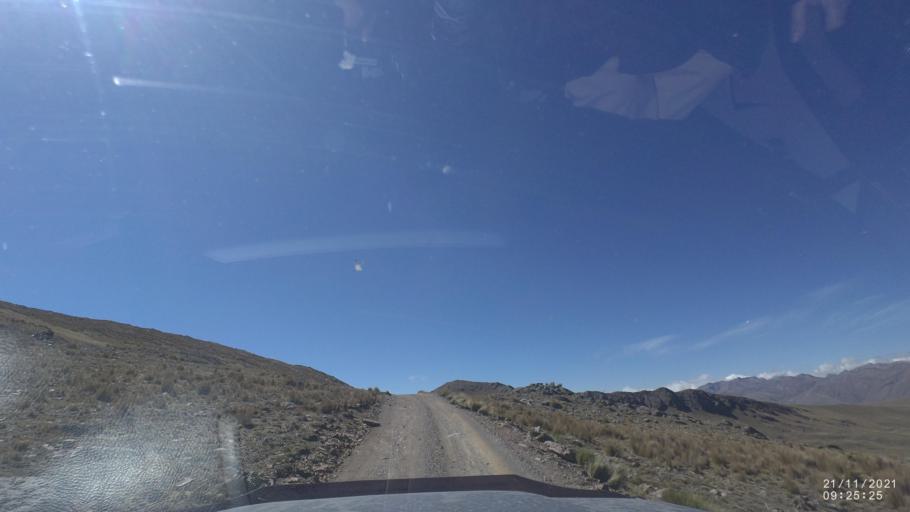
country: BO
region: Cochabamba
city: Cochabamba
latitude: -17.0906
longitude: -66.2547
